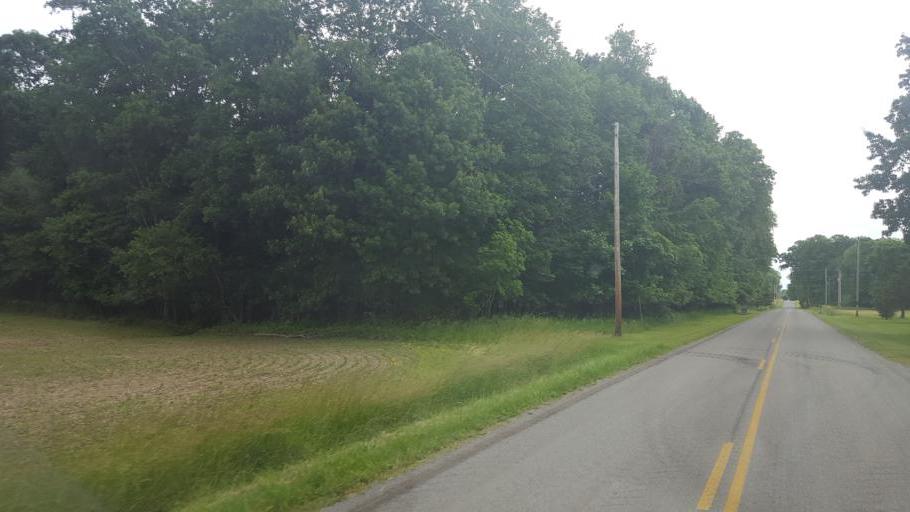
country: US
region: Ohio
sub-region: Wyandot County
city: Upper Sandusky
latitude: 40.7747
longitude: -83.1909
